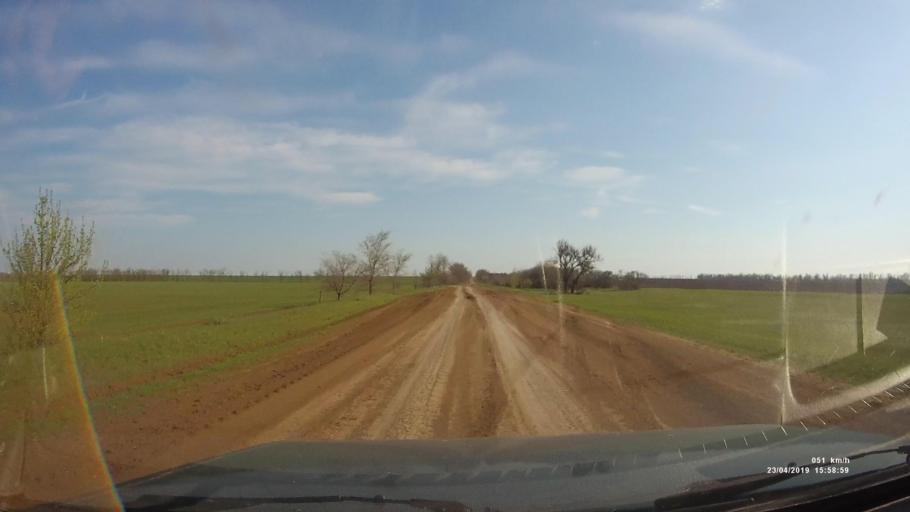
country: RU
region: Rostov
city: Remontnoye
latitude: 46.5199
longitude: 43.1099
